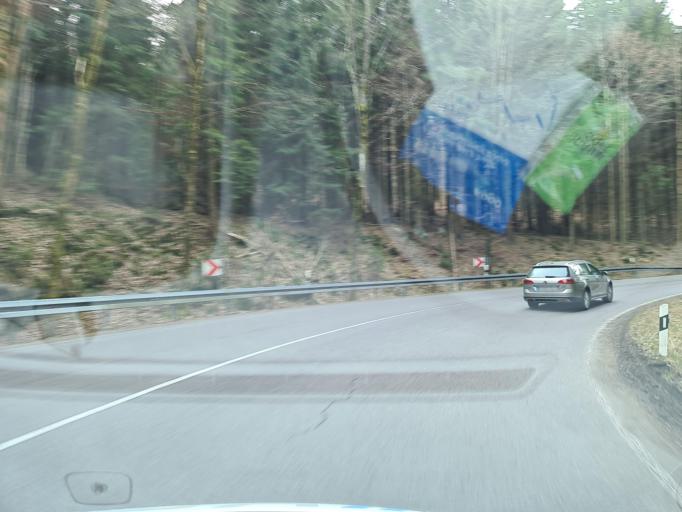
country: DE
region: Saxony
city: Lengefeld
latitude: 50.7011
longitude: 13.2007
